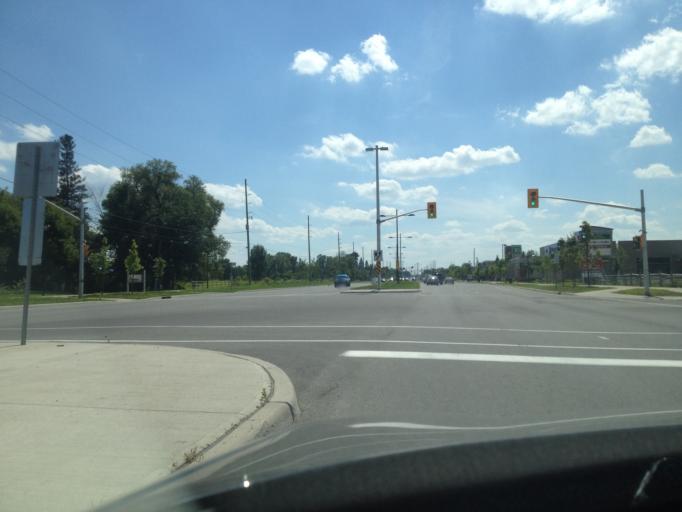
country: CA
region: Ontario
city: Bells Corners
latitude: 45.2854
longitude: -75.9085
